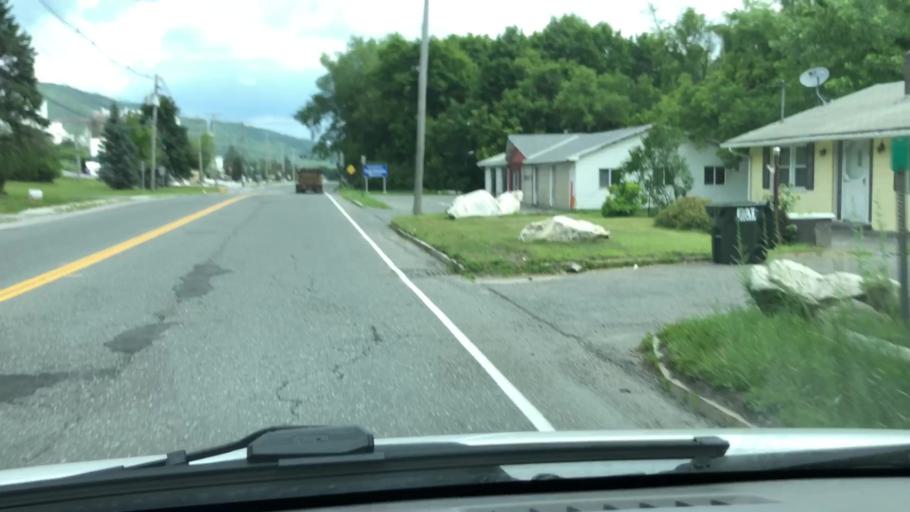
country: US
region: Massachusetts
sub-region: Berkshire County
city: Adams
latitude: 42.6402
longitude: -73.1122
